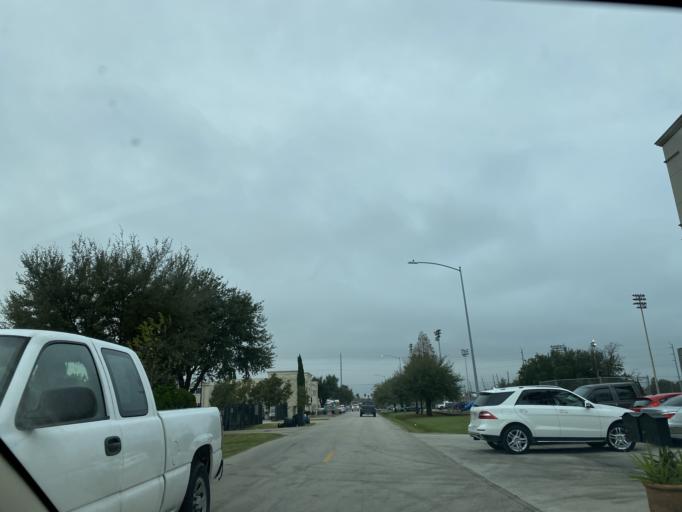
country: US
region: Texas
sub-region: Harris County
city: Bellaire
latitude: 29.7289
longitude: -95.4777
